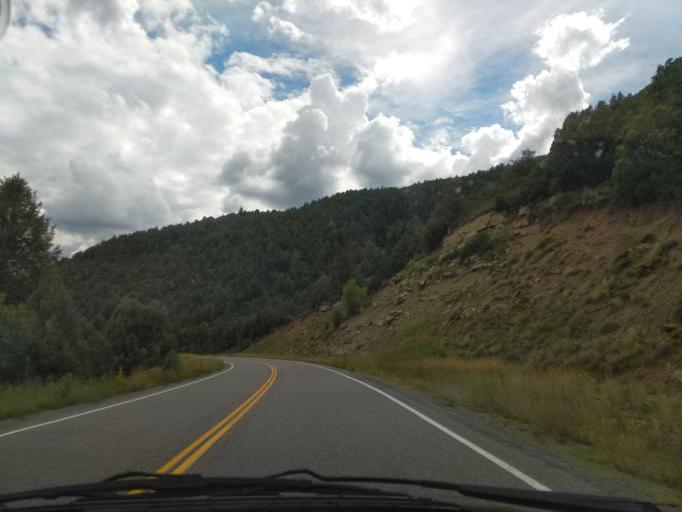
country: US
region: Colorado
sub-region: Delta County
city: Paonia
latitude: 39.0202
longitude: -107.3631
